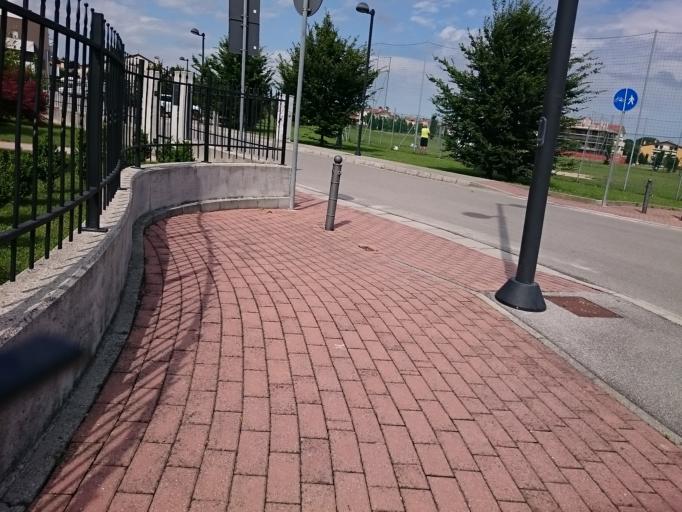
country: IT
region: Veneto
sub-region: Provincia di Padova
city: Caselle
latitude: 45.4121
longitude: 11.8181
